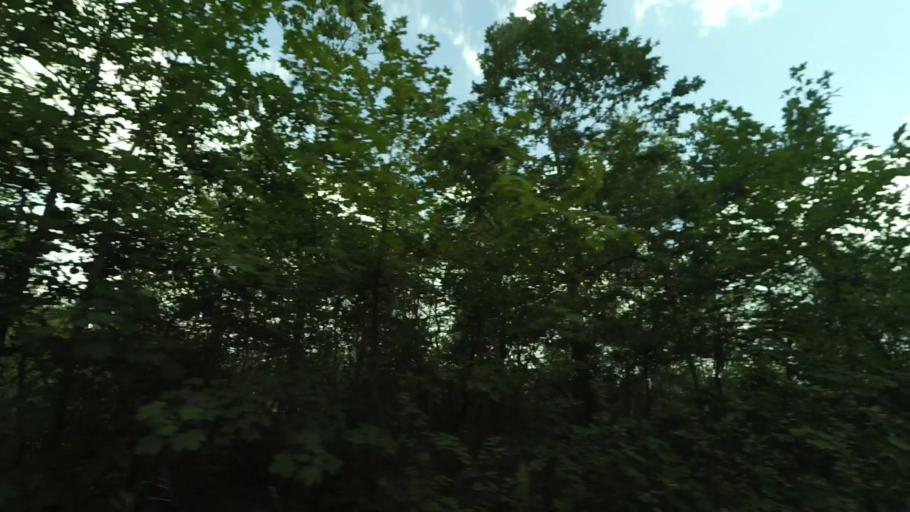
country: DK
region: Central Jutland
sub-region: Norddjurs Kommune
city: Auning
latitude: 56.5111
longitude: 10.4130
